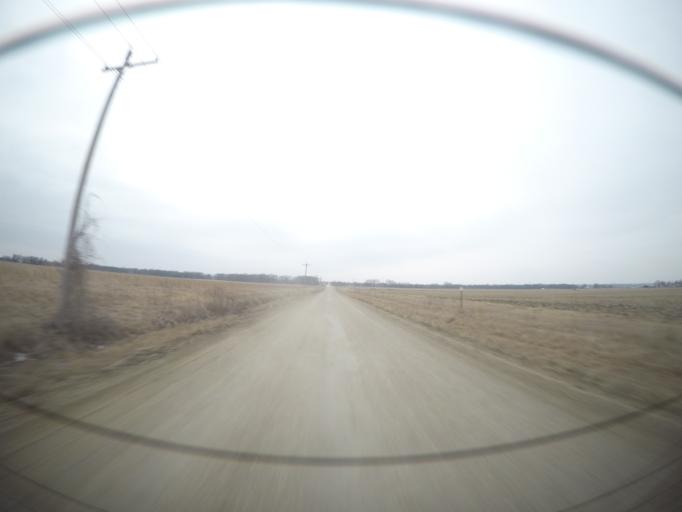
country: US
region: Kansas
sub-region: Pottawatomie County
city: Wamego
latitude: 39.1521
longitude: -96.3017
